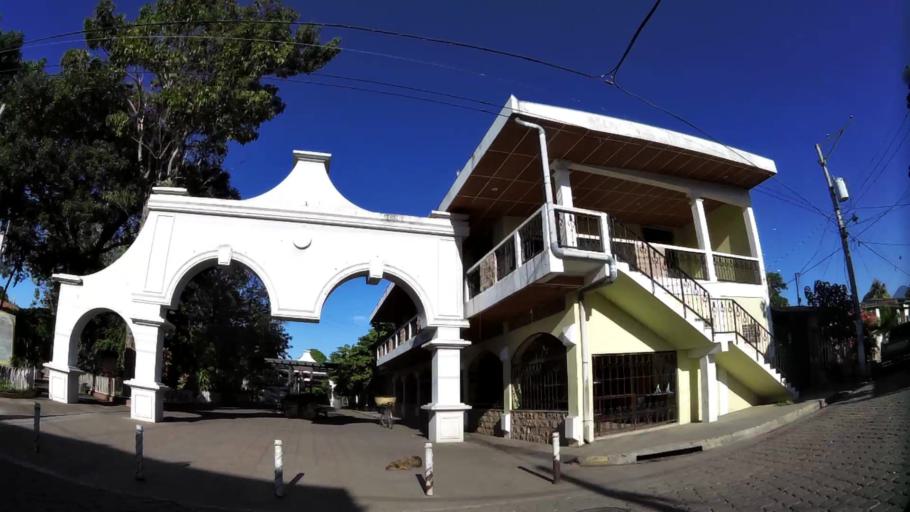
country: SV
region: Sonsonate
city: Sonsonate
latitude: 13.7043
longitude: -89.7150
